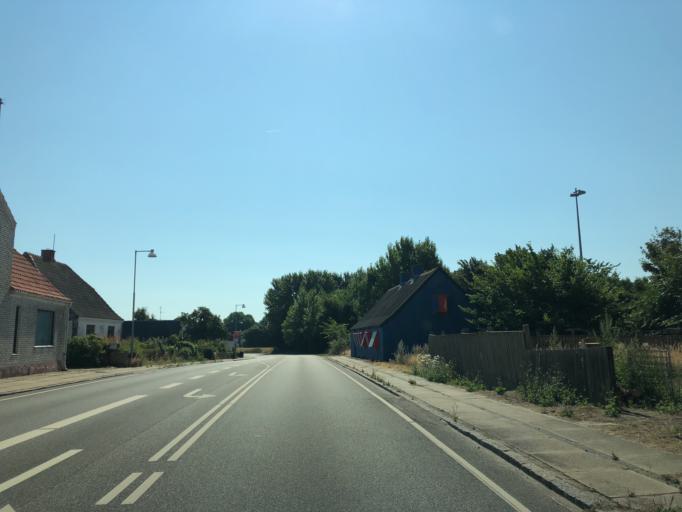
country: DK
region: Zealand
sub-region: Odsherred Kommune
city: Asnaes
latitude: 55.9648
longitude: 11.3696
